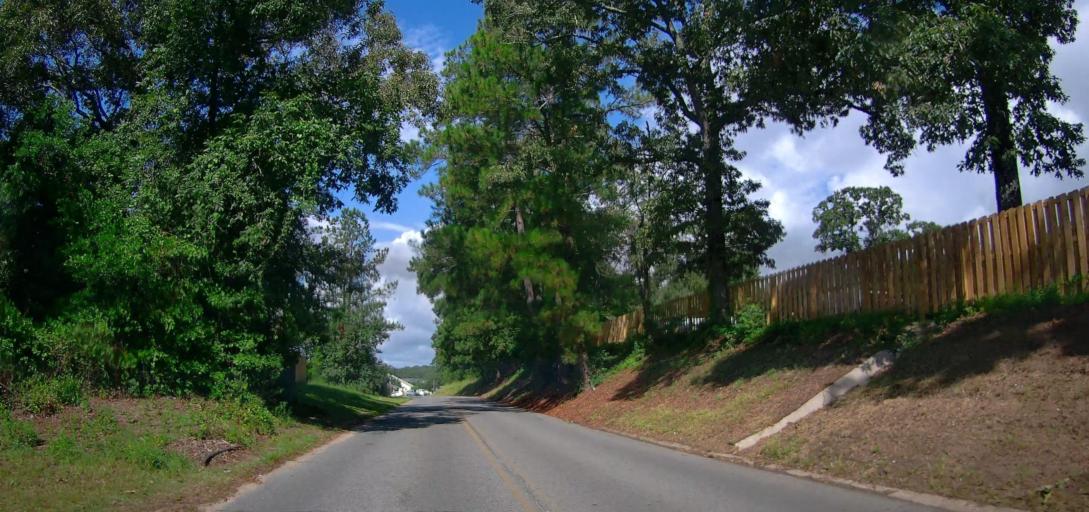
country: US
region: Georgia
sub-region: Houston County
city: Warner Robins
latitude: 32.5856
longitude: -83.6243
